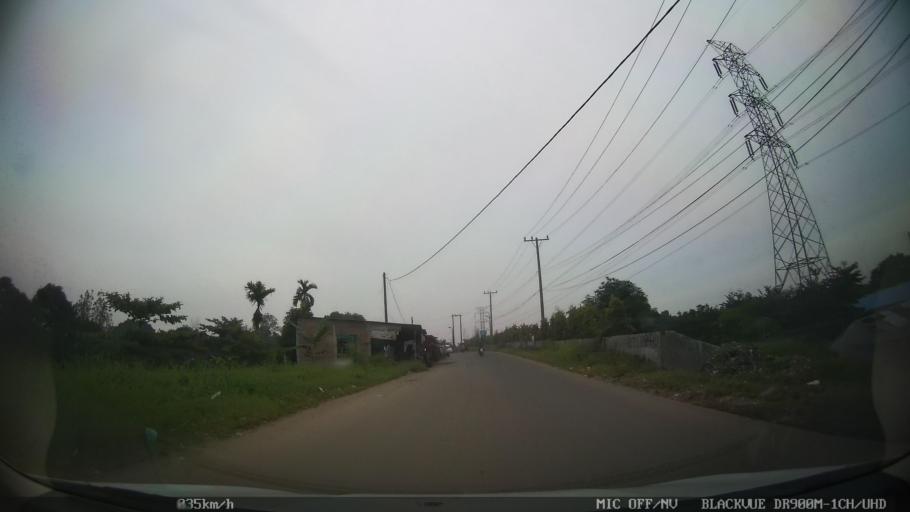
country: ID
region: North Sumatra
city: Deli Tua
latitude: 3.5515
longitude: 98.7265
